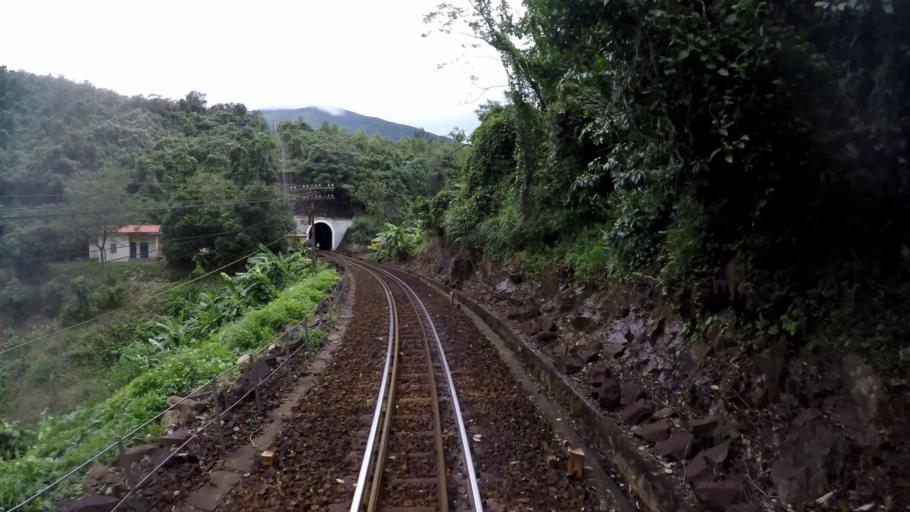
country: VN
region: Da Nang
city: Lien Chieu
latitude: 16.1721
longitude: 108.1442
